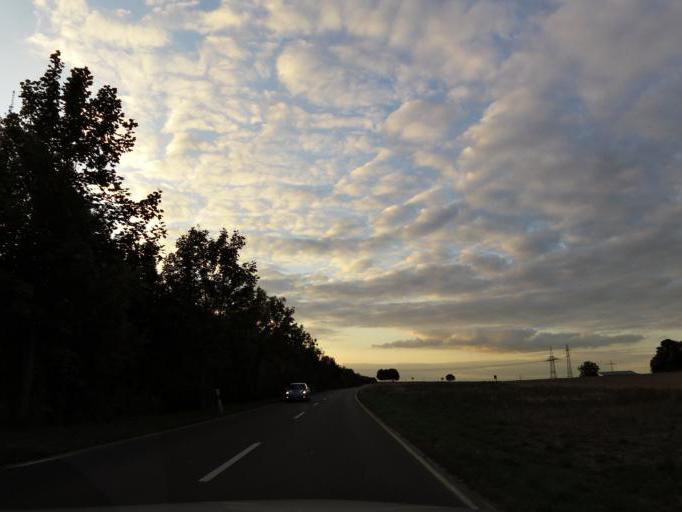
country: DE
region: Rheinland-Pfalz
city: Dexheim
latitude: 49.8457
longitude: 8.3105
